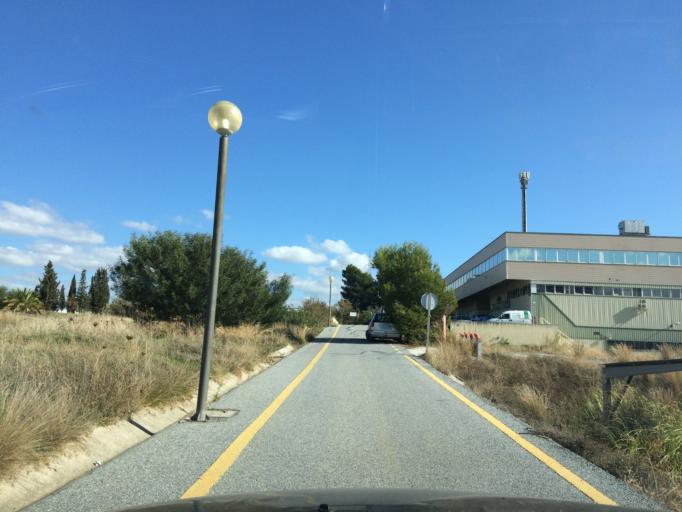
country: ES
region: Andalusia
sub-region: Provincia de Malaga
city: Estacion de Cartama
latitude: 36.7346
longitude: -4.5496
